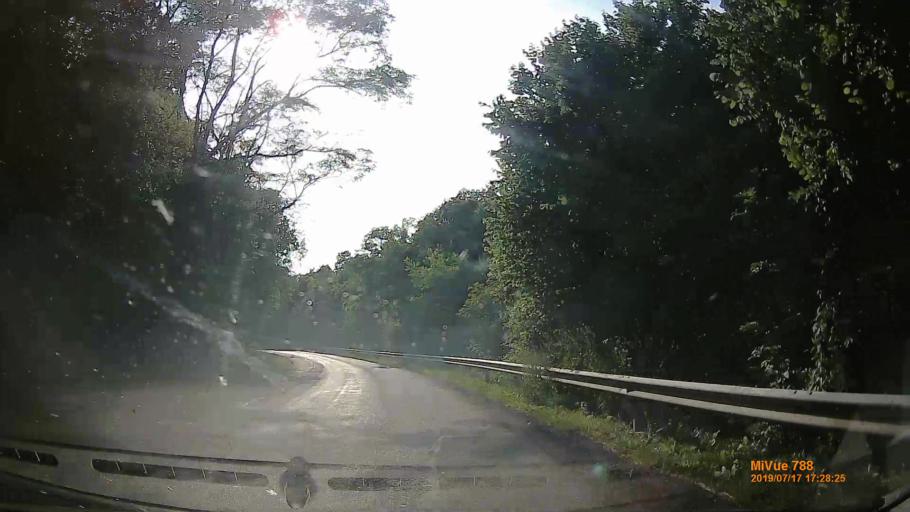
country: HU
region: Veszprem
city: Urkut
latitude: 47.0087
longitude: 17.5967
